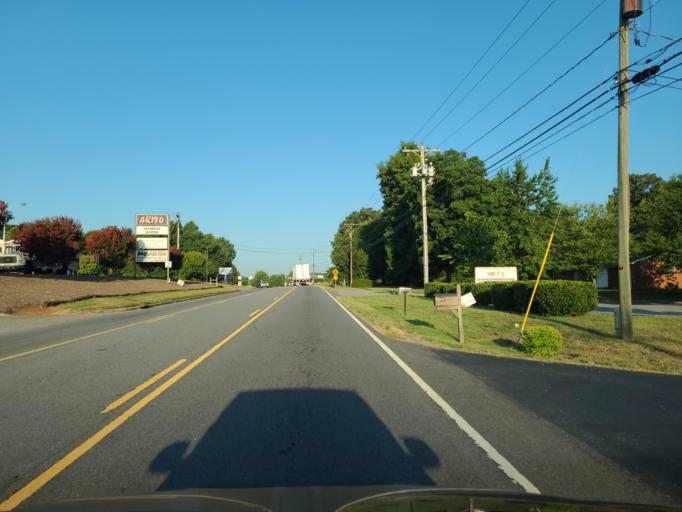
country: US
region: North Carolina
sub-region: Catawba County
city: Mountain View
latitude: 35.6861
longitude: -81.3705
